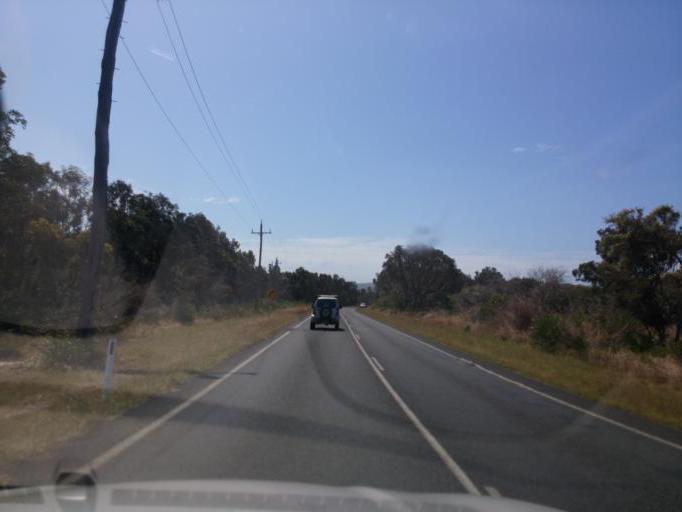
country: AU
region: New South Wales
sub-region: Great Lakes
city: Forster
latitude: -32.2516
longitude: 152.5365
